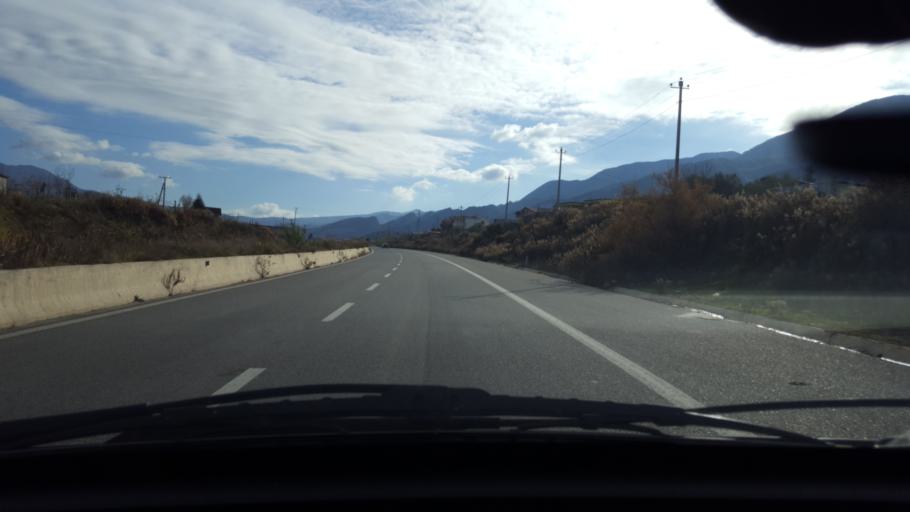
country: AL
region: Tirane
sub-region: Rrethi i Tiranes
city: Berzhite
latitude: 41.2542
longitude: 19.8926
